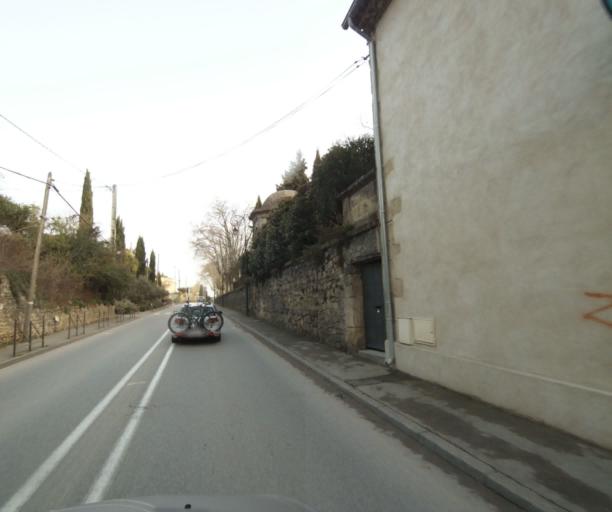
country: FR
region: Provence-Alpes-Cote d'Azur
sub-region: Departement des Bouches-du-Rhone
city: Rognes
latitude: 43.6625
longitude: 5.3499
